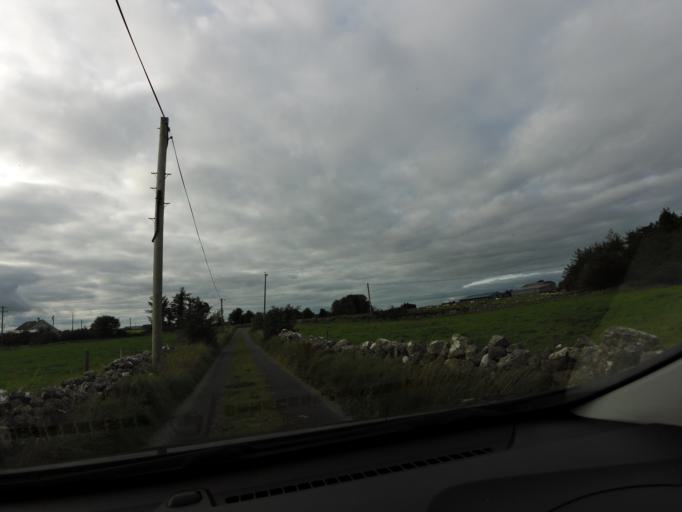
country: IE
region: Connaught
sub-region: County Galway
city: Ballinasloe
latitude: 53.3600
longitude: -8.0965
